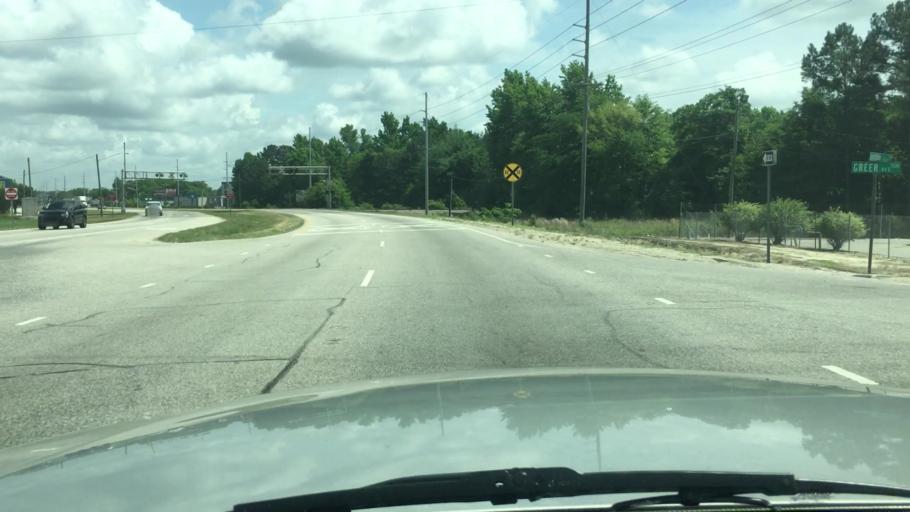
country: US
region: North Carolina
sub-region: Cumberland County
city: Fayetteville
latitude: 35.0382
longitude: -78.8672
